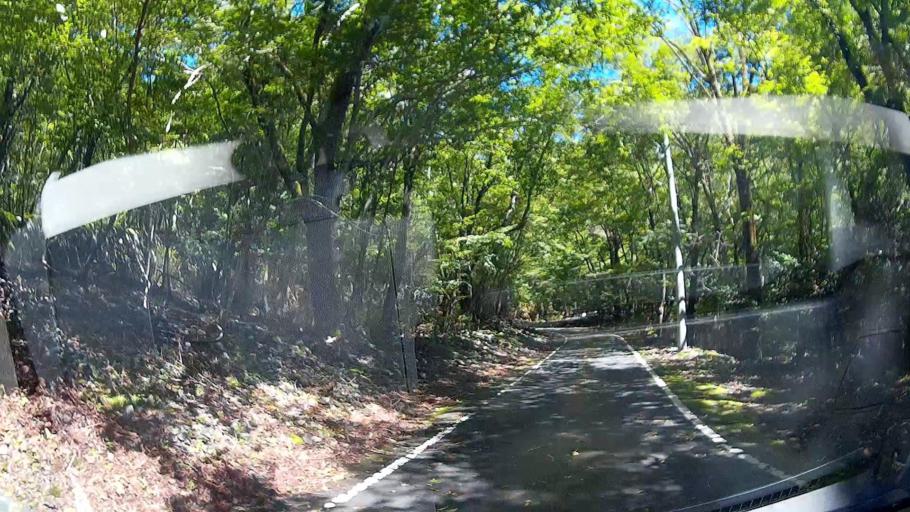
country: JP
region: Shizuoka
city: Fujinomiya
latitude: 35.3007
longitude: 138.3135
